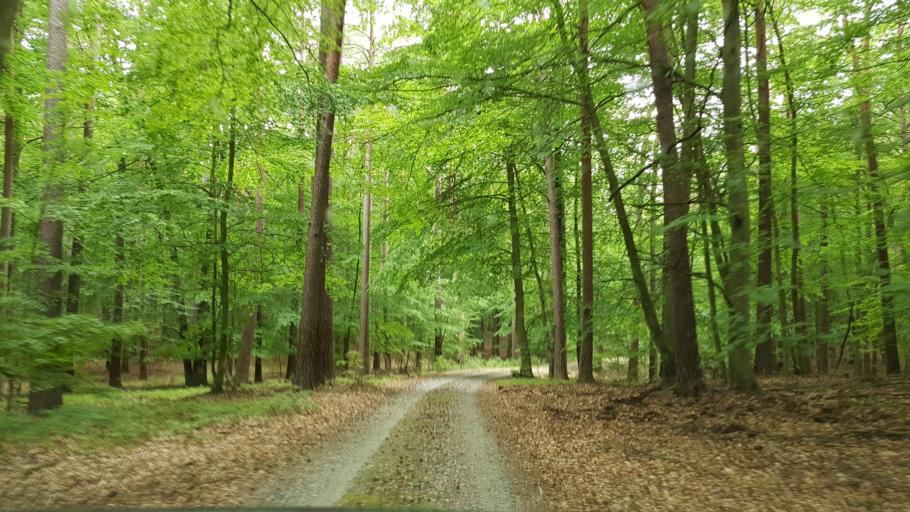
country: PL
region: West Pomeranian Voivodeship
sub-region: Powiat kamienski
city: Miedzyzdroje
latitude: 53.9406
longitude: 14.4924
